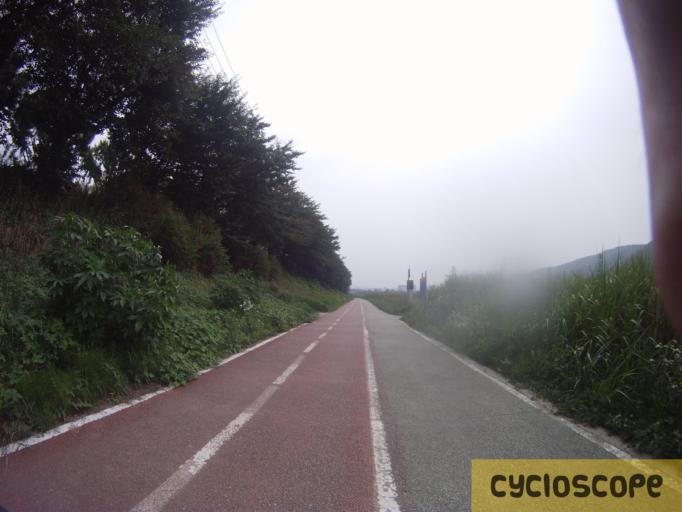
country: KR
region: Gyeonggi-do
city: Anyang-si
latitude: 37.4347
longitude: 126.9007
